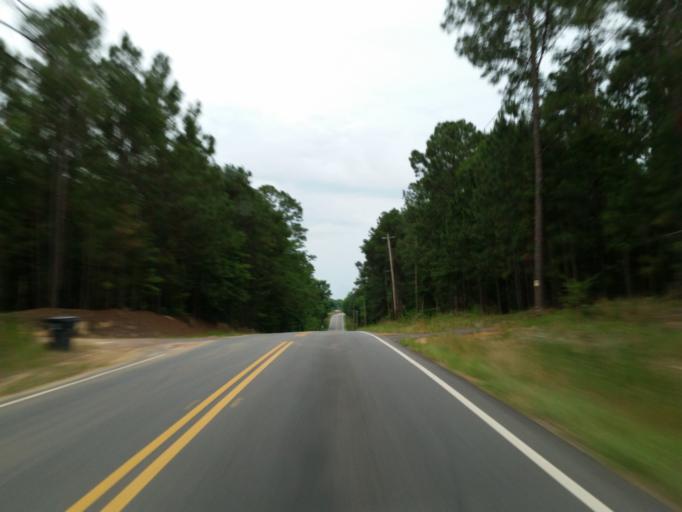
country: US
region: Georgia
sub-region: Crisp County
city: Cordele
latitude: 31.8813
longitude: -83.7539
